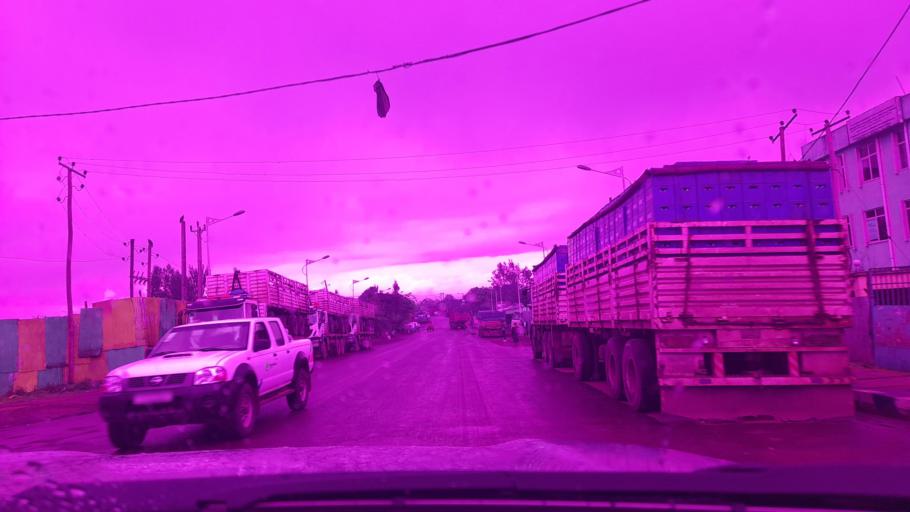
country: ET
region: Oromiya
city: Jima
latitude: 7.6731
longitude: 36.8519
